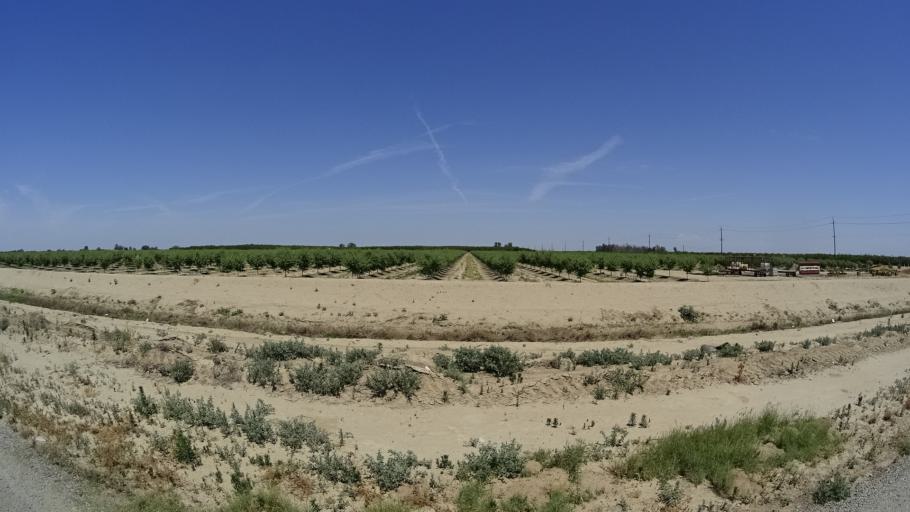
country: US
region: California
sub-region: Kings County
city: Armona
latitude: 36.2404
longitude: -119.6924
